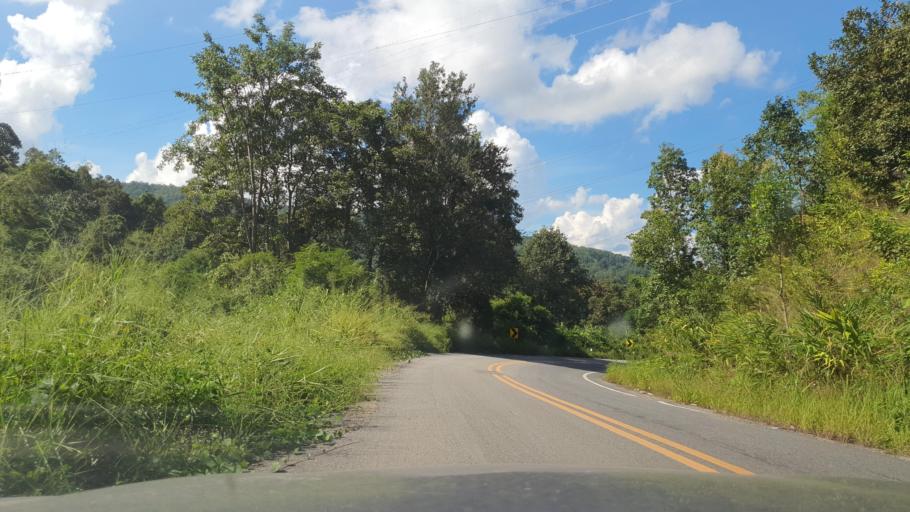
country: TH
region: Chiang Rai
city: Wiang Pa Pao
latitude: 19.3283
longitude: 99.4484
